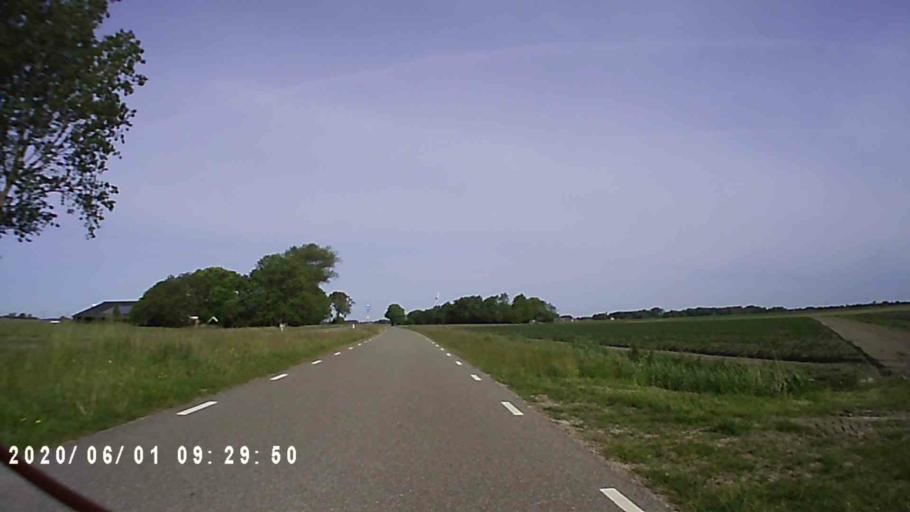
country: NL
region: Friesland
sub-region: Gemeente Leeuwarderadeel
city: Stiens
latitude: 53.2657
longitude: 5.7330
